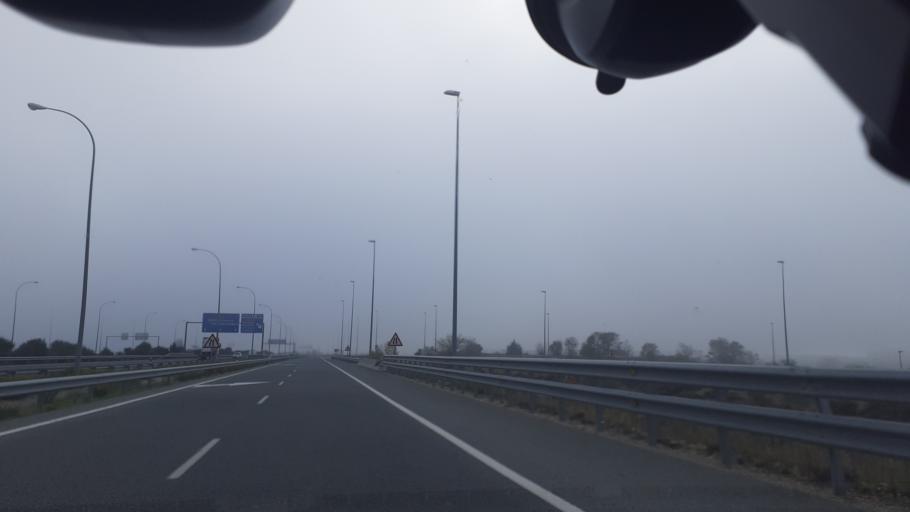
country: ES
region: Madrid
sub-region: Provincia de Madrid
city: Vicalvaro
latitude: 40.4003
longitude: -3.5746
